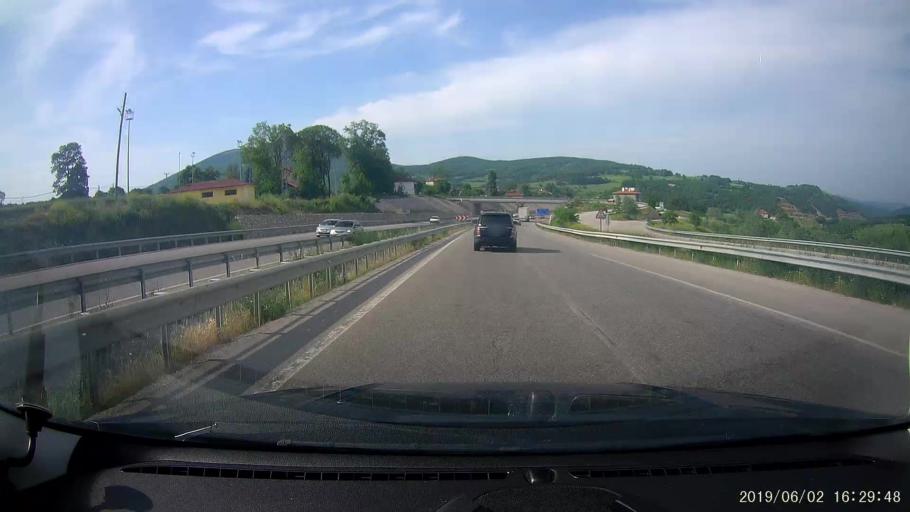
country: TR
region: Samsun
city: Ladik
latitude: 41.0177
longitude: 35.8723
